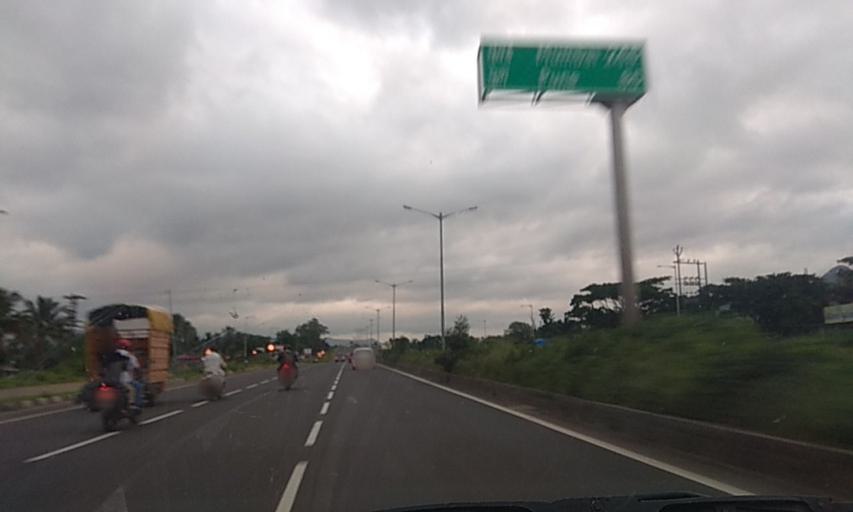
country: IN
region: Maharashtra
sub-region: Satara Division
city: Wai
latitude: 17.8987
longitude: 73.9716
